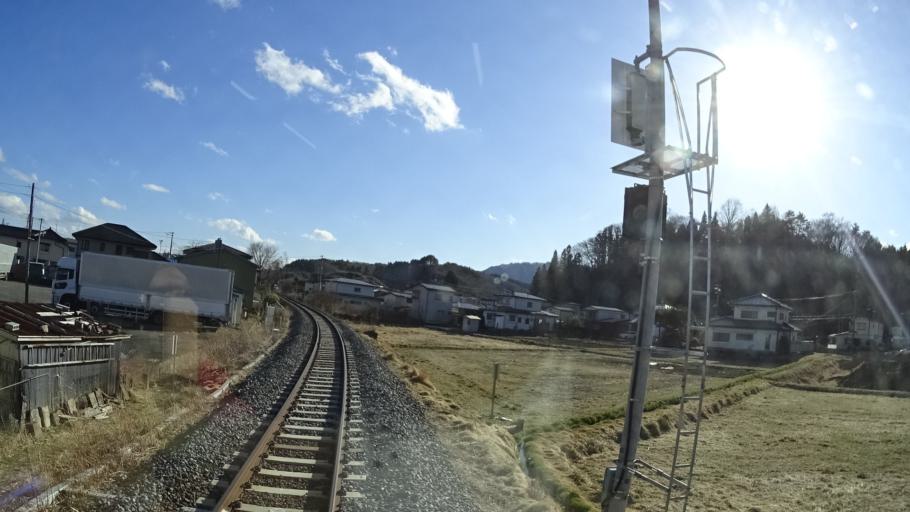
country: JP
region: Iwate
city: Miyako
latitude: 39.5780
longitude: 141.9355
